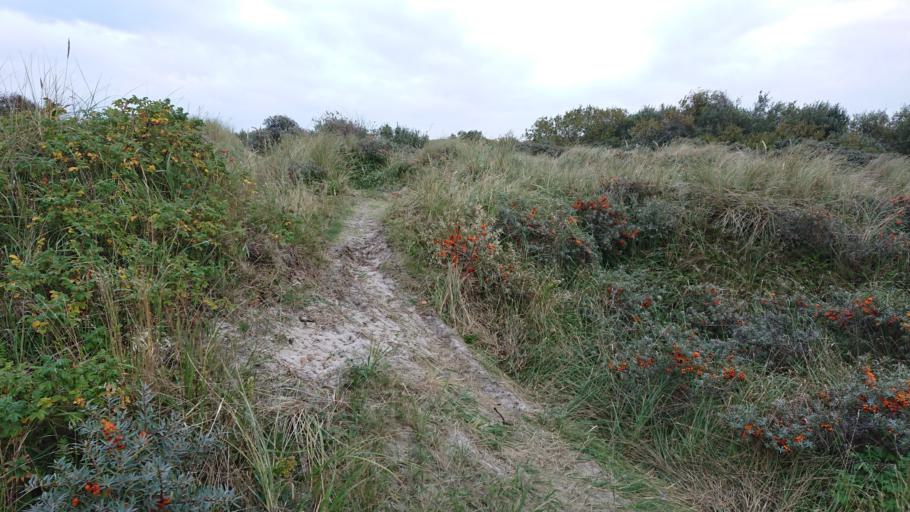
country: DK
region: North Denmark
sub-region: Frederikshavn Kommune
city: Skagen
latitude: 57.7464
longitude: 10.6279
